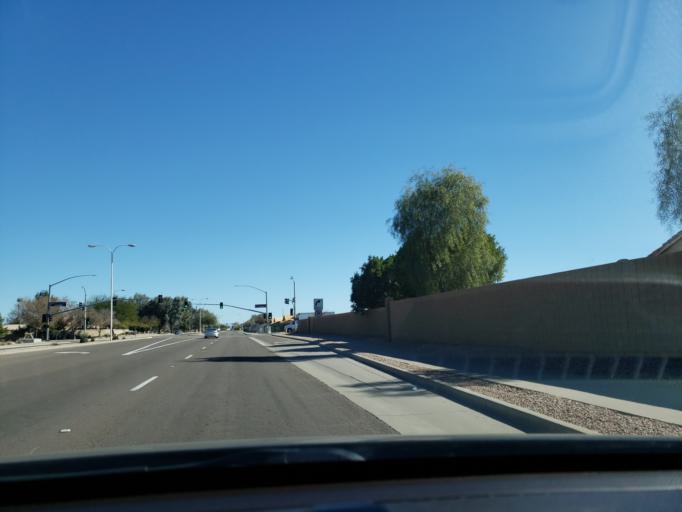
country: US
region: Arizona
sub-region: Maricopa County
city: Chandler
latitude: 33.3206
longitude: -111.8297
